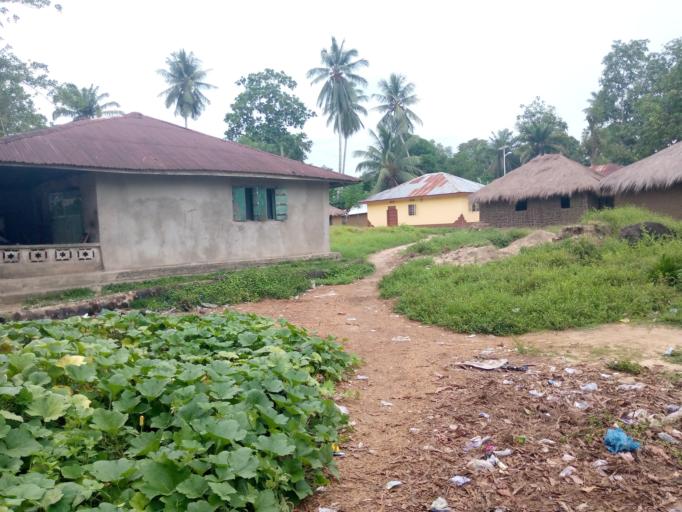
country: SL
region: Southern Province
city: Bonthe
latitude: 7.5223
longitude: -12.5010
